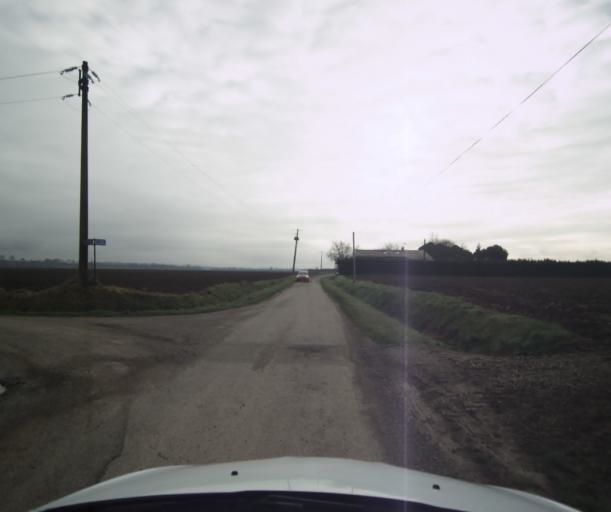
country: FR
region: Midi-Pyrenees
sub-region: Departement du Tarn-et-Garonne
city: Castelsarrasin
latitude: 44.0248
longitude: 1.1237
